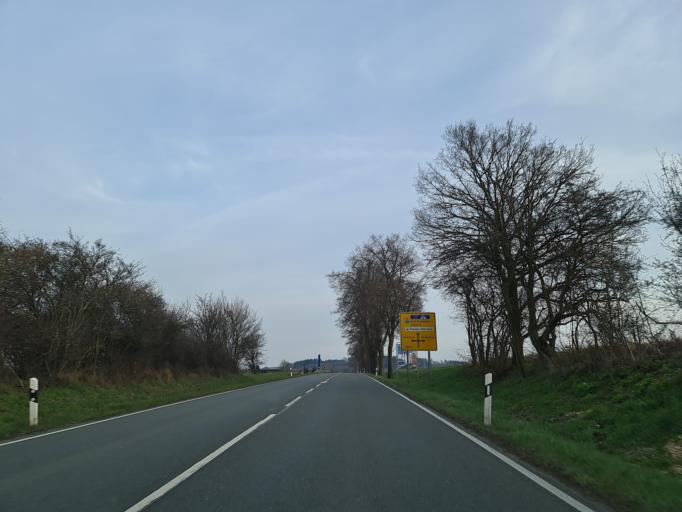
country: DE
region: Saxony
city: Plauen
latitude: 50.4618
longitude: 12.1554
